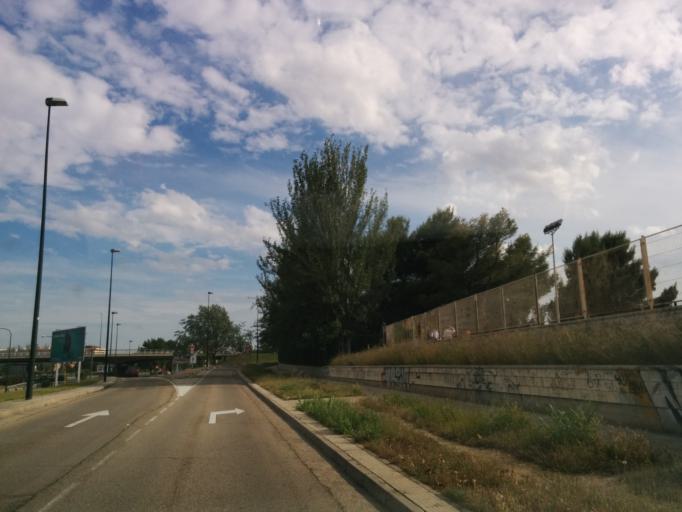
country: ES
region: Aragon
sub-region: Provincia de Zaragoza
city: Zaragoza
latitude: 41.6748
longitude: -0.8814
